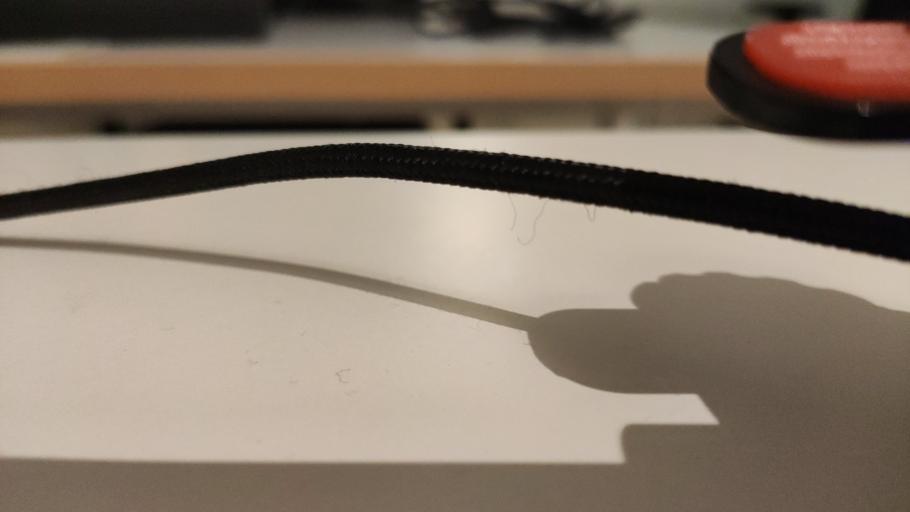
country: RU
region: Moskovskaya
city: Rogachevo
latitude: 56.4124
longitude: 37.2223
